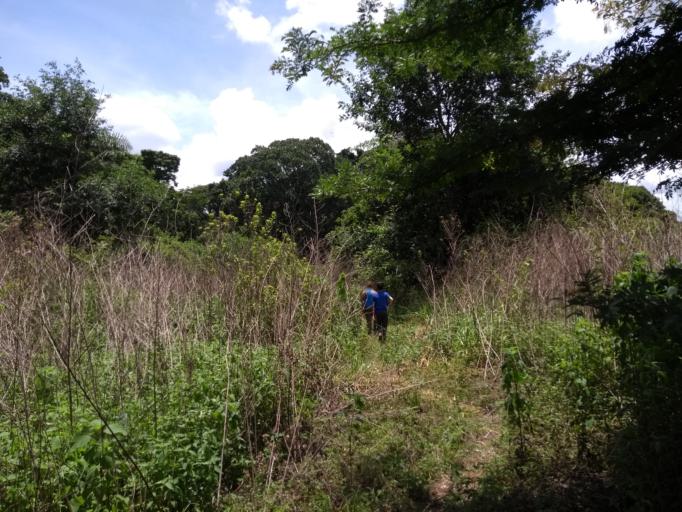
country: BR
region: Goias
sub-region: Formosa
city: Formosa
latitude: -15.4971
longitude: -47.3013
